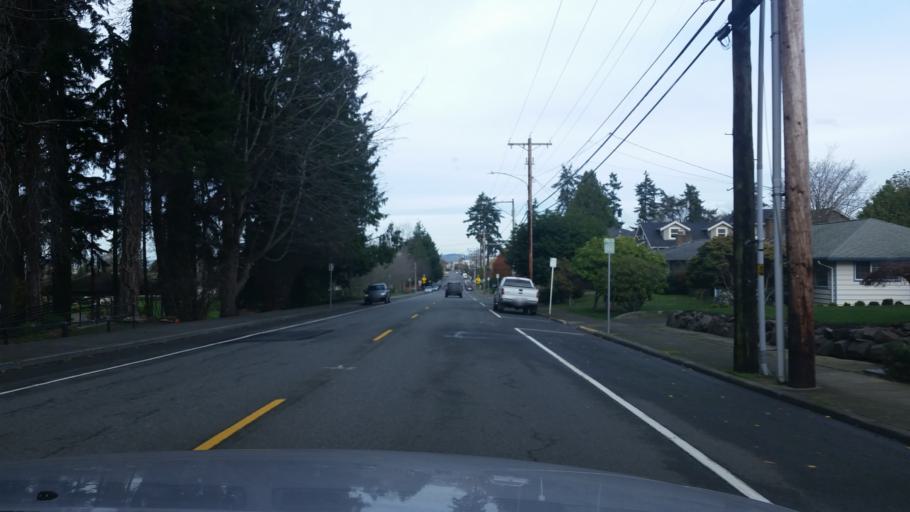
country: US
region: Washington
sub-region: Snohomish County
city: Edmonds
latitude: 47.8043
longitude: -122.3802
